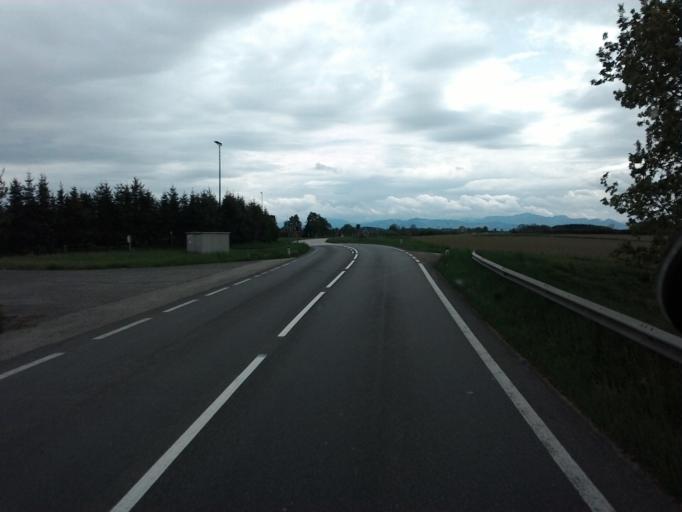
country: AT
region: Upper Austria
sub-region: Wels-Land
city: Sattledt
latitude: 48.0487
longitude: 14.0584
